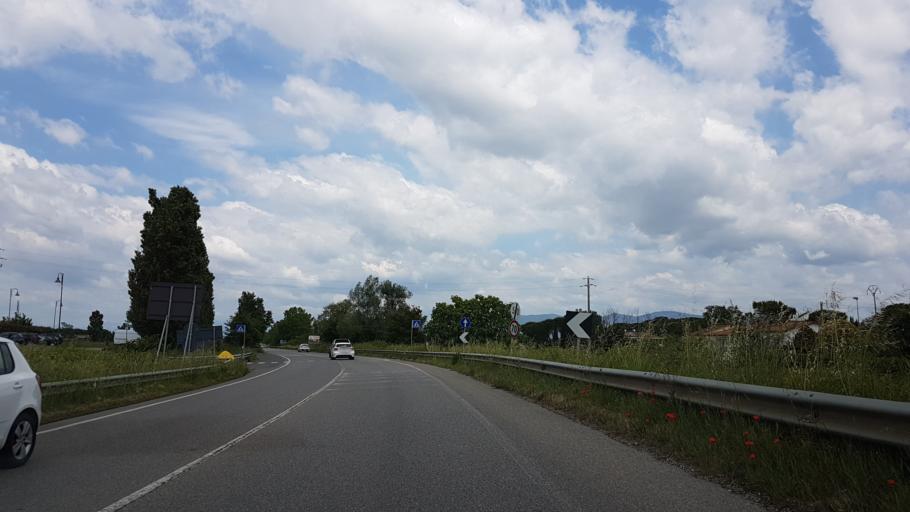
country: IT
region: Tuscany
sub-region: Provincia di Livorno
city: Collesalvetti
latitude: 43.6017
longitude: 10.4755
